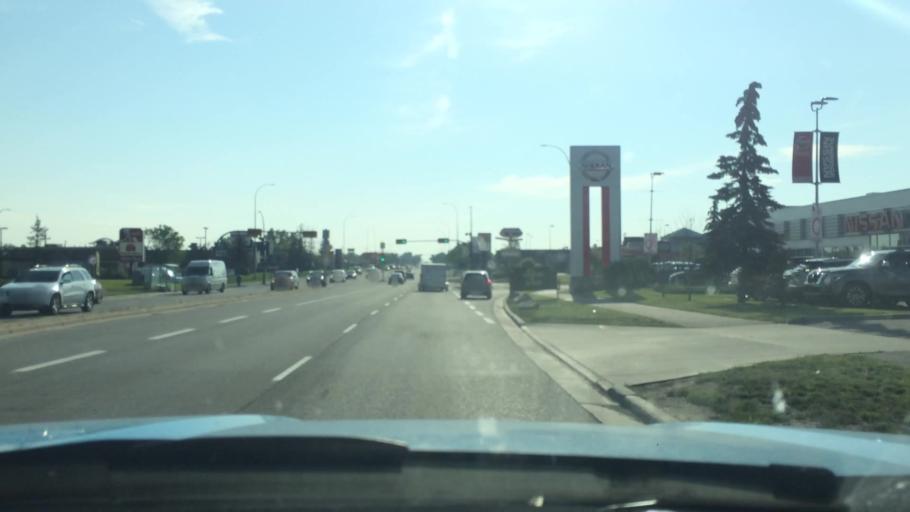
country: CA
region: Alberta
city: Calgary
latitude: 51.0814
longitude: -113.9902
